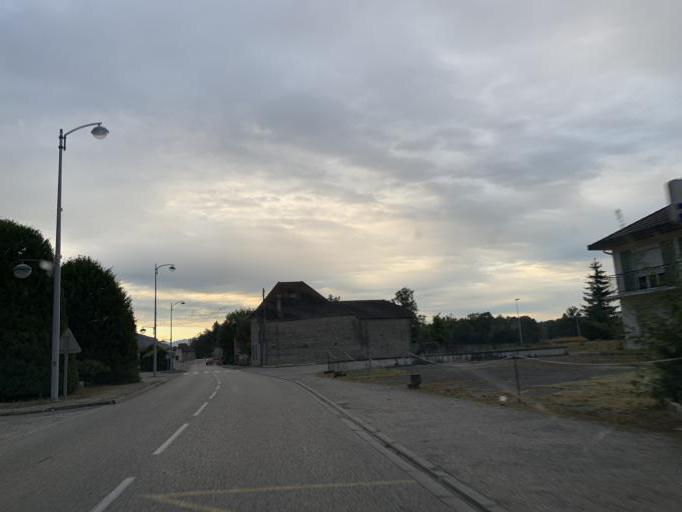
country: FR
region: Rhone-Alpes
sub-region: Departement de l'Isere
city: Les Avenieres
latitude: 45.6942
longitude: 5.5877
